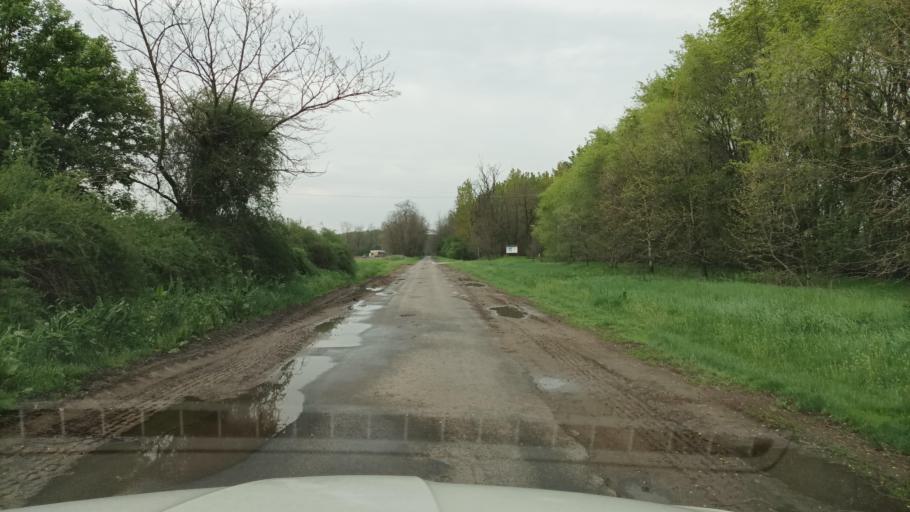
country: HU
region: Pest
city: Nagykoros
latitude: 46.9810
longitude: 19.8080
